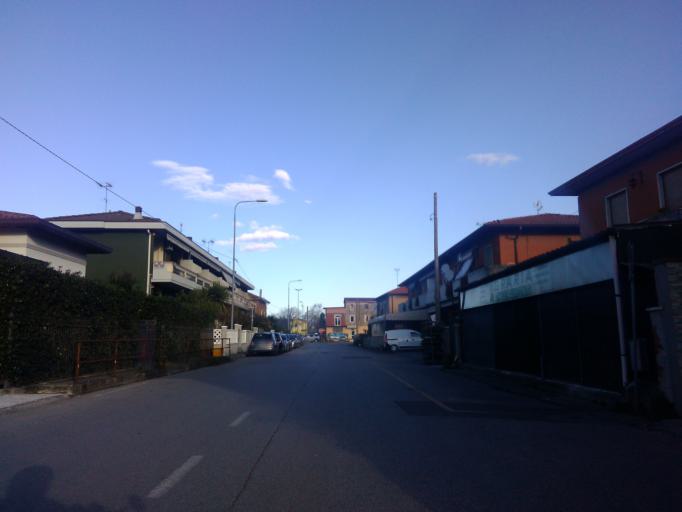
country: IT
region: Tuscany
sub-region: Provincia di Massa-Carrara
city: Carrara
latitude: 44.0578
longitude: 10.0472
